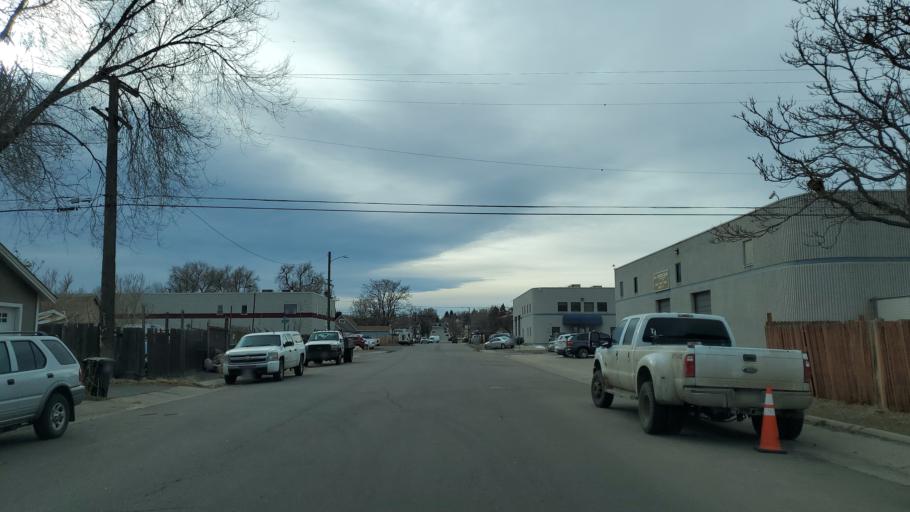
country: US
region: Colorado
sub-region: Denver County
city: Denver
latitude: 39.7137
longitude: -105.0087
